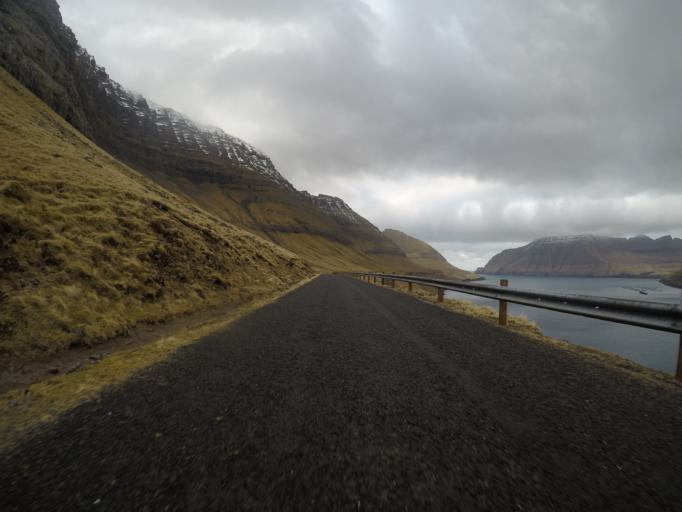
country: FO
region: Nordoyar
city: Klaksvik
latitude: 62.3294
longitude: -6.5707
